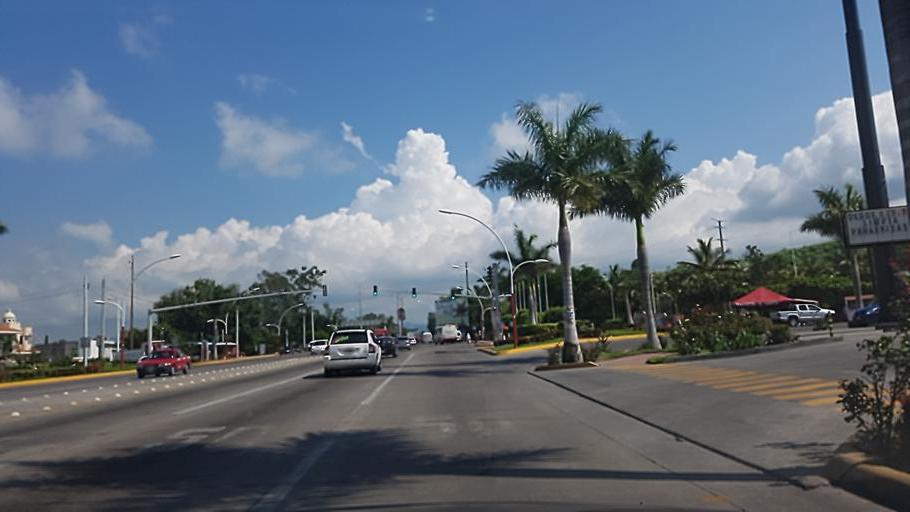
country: MX
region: Nayarit
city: Xalisco
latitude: 21.4732
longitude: -104.8897
